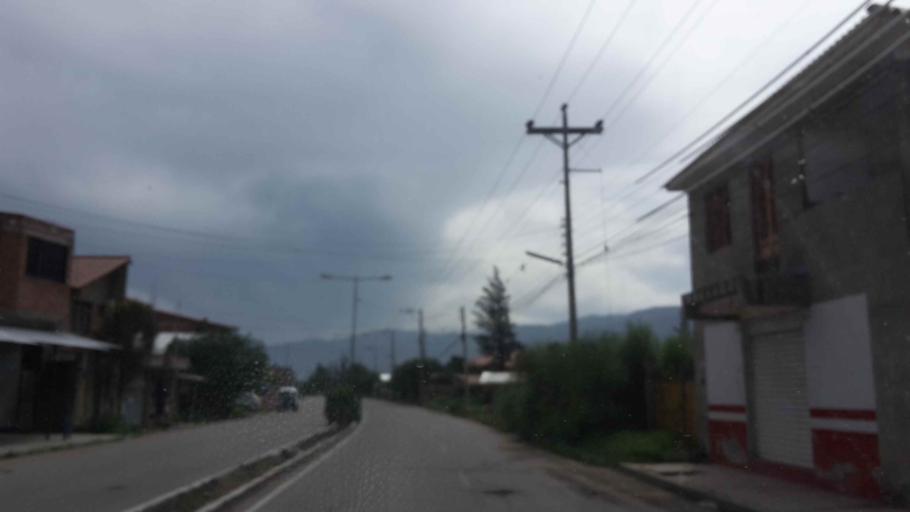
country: BO
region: Cochabamba
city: Cochabamba
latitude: -17.3326
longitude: -66.2514
